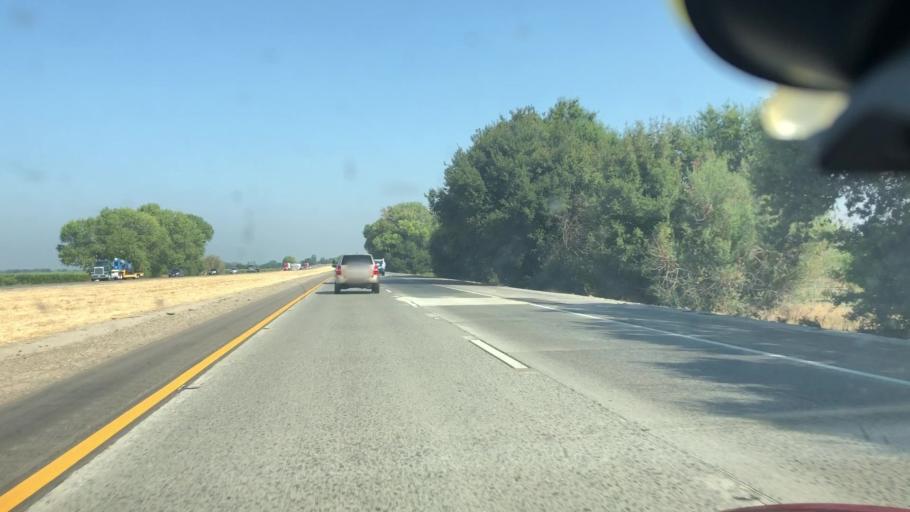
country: US
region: California
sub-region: San Joaquin County
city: Thornton
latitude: 38.2378
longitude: -121.4390
